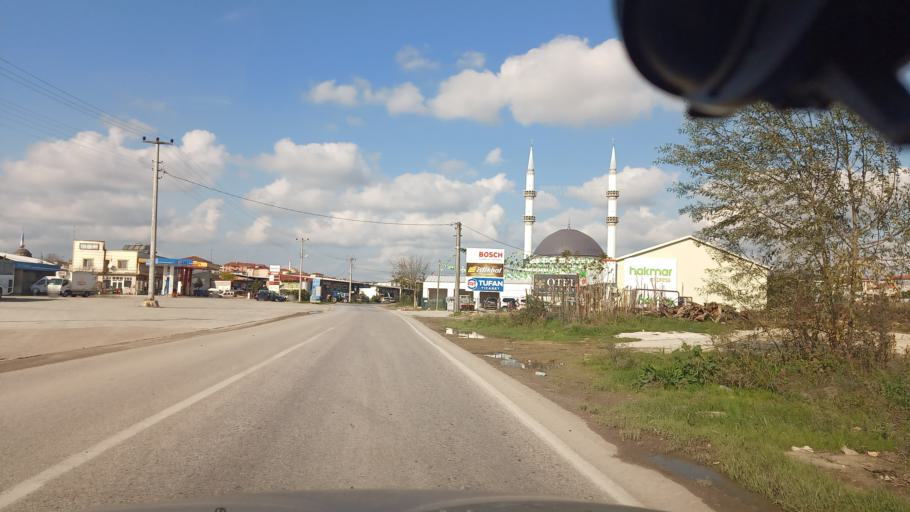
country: TR
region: Sakarya
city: Kaynarca
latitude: 41.0253
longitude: 30.3096
